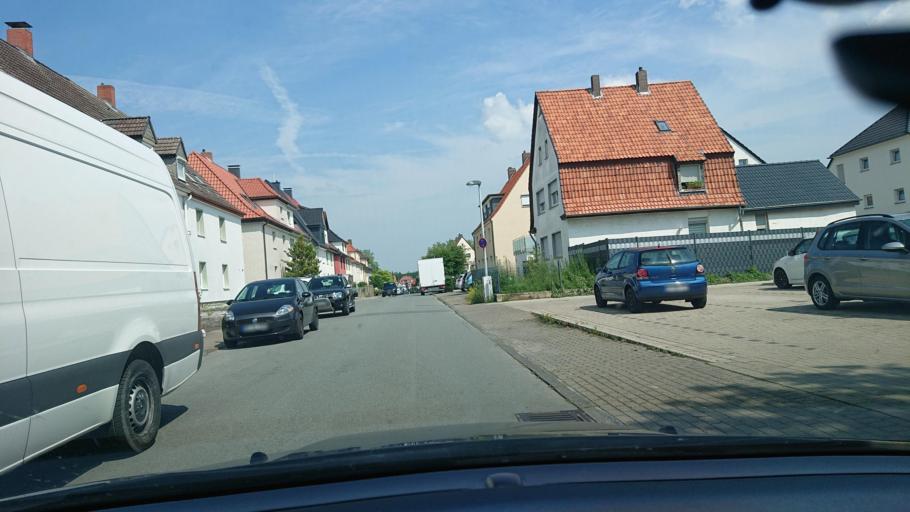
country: DE
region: North Rhine-Westphalia
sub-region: Regierungsbezirk Arnsberg
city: Soest
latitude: 51.5647
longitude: 8.1259
